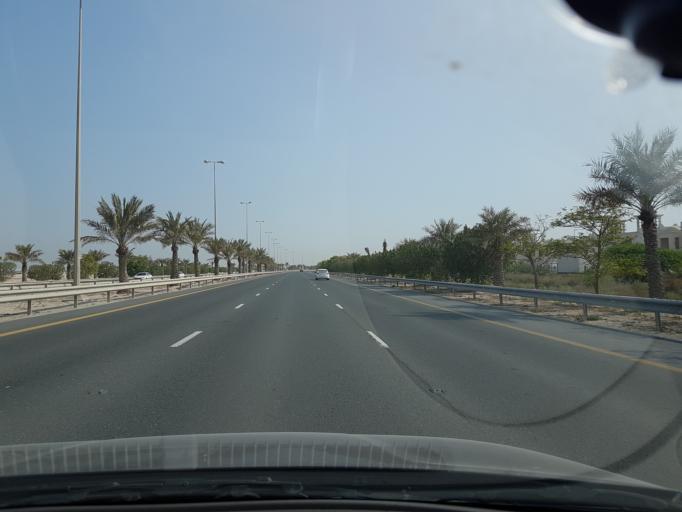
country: BH
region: Central Governorate
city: Dar Kulayb
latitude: 26.0883
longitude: 50.5394
